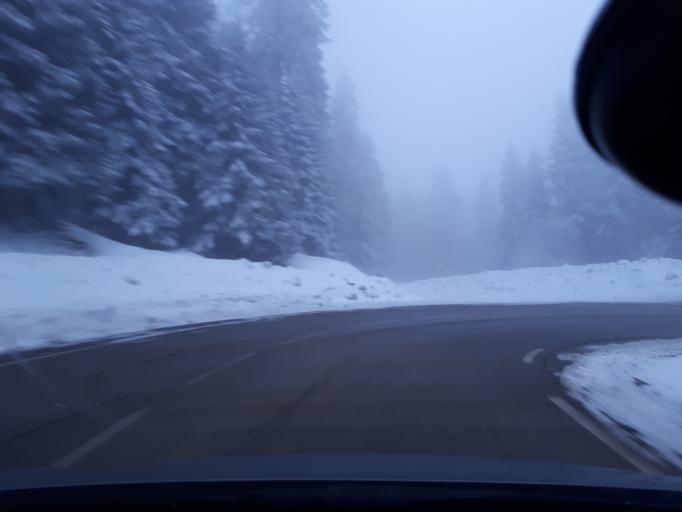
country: FR
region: Rhone-Alpes
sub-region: Departement de l'Isere
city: Vaulnaveys-le-Bas
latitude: 45.0891
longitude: 5.8577
